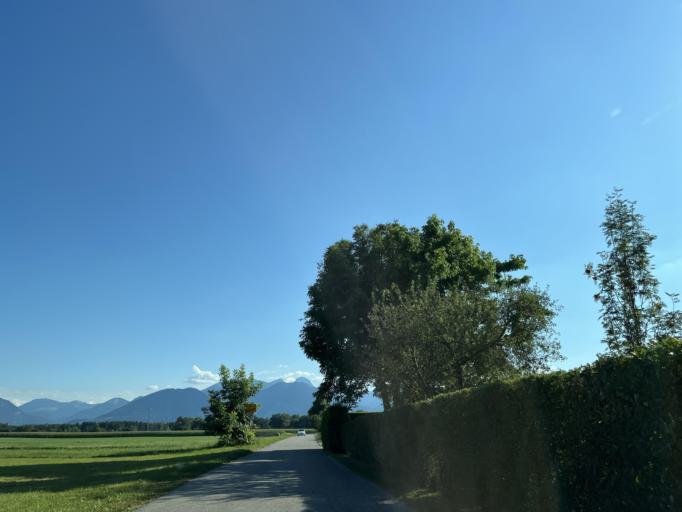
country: DE
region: Bavaria
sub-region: Upper Bavaria
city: Kolbermoor
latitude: 47.8198
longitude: 12.0781
